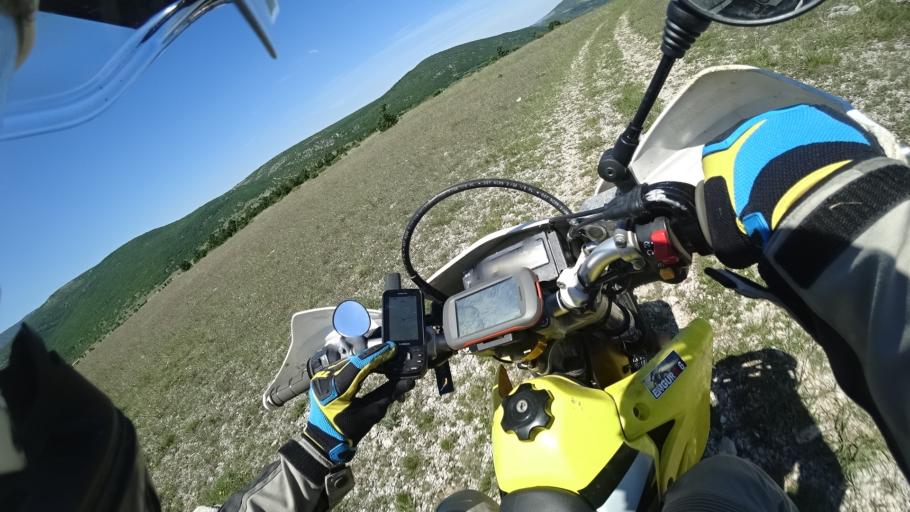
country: HR
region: Sibensko-Kniniska
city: Knin
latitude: 44.0172
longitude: 16.3549
